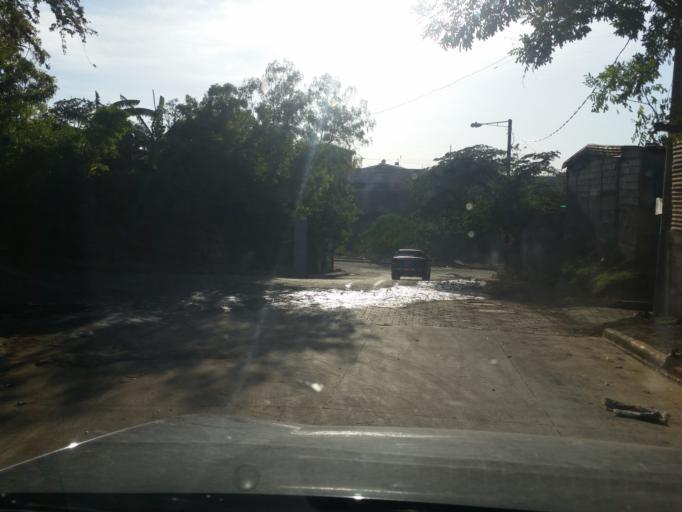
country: NI
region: Managua
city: Managua
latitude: 12.1105
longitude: -86.2408
